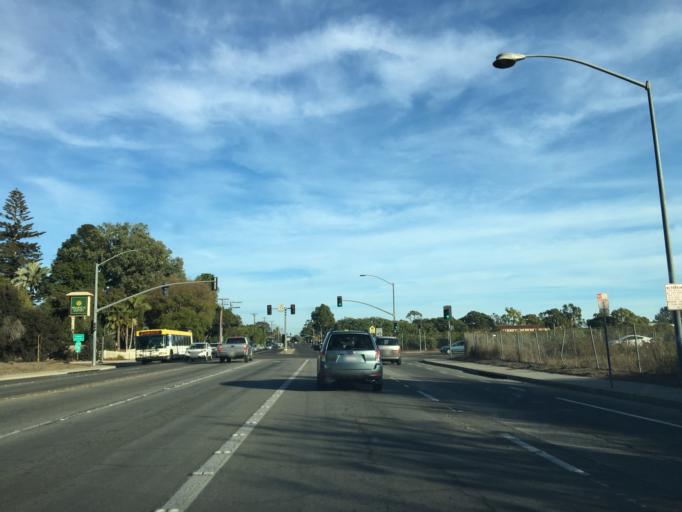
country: US
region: California
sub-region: Santa Barbara County
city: Goleta
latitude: 34.4353
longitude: -119.8177
